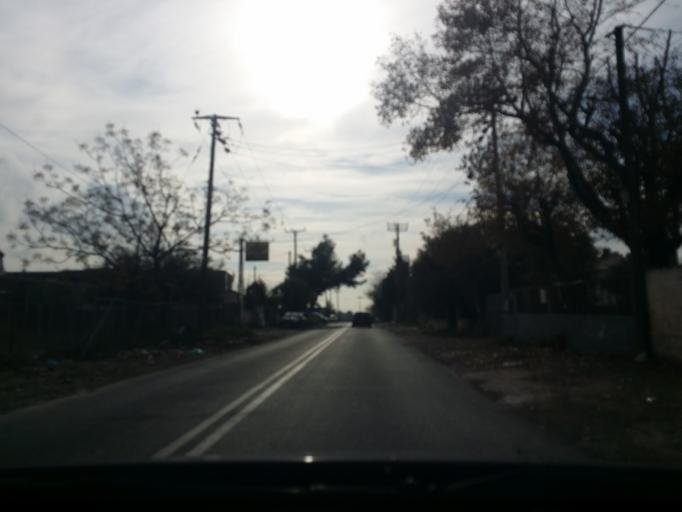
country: GR
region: Attica
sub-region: Nomarchia Athinas
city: Metamorfosi
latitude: 38.0805
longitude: 23.7644
